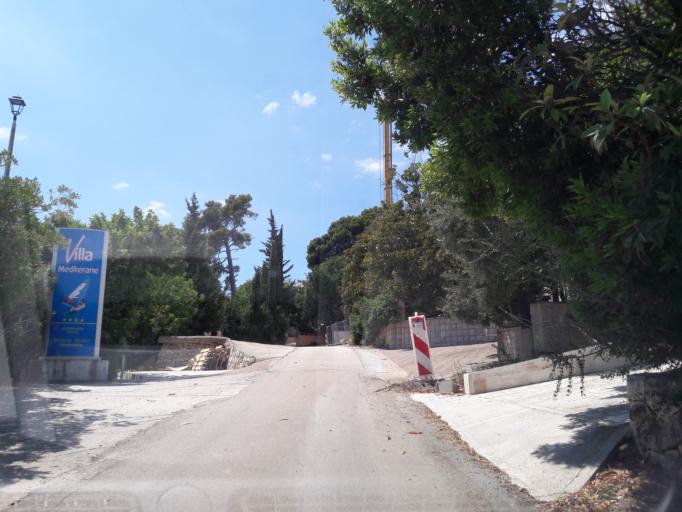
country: HR
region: Dubrovacko-Neretvanska
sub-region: Grad Korcula
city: Zrnovo
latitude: 42.9838
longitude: 17.0858
